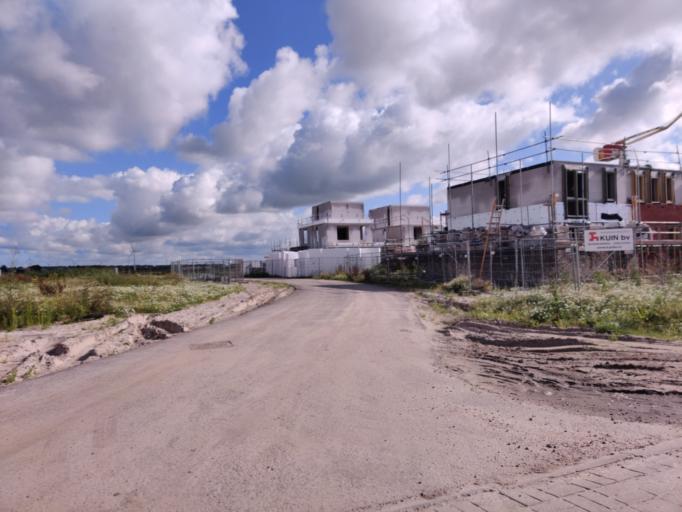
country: NL
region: Flevoland
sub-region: Gemeente Zeewolde
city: Zeewolde
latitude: 52.3485
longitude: 5.5305
